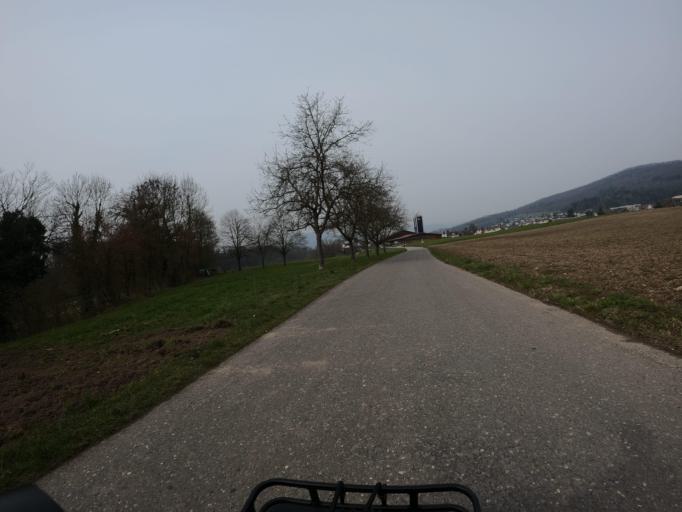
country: CH
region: Aargau
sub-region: Bezirk Lenzburg
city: Niederlenz
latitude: 47.4102
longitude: 8.1897
